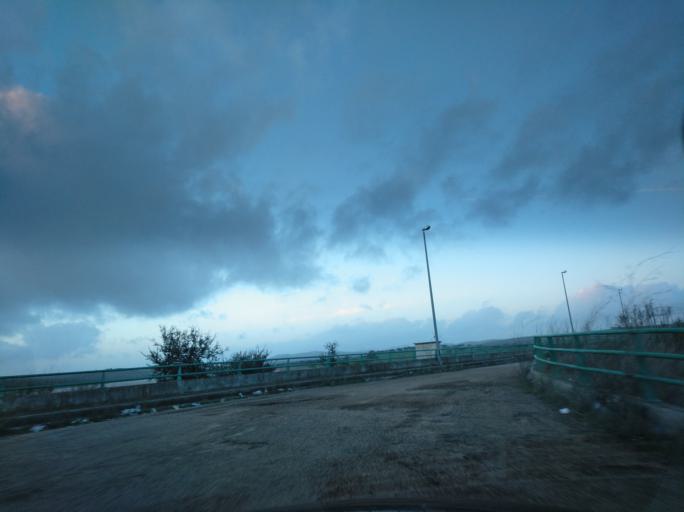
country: PT
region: Portalegre
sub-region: Campo Maior
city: Campo Maior
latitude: 39.0942
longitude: -7.1215
